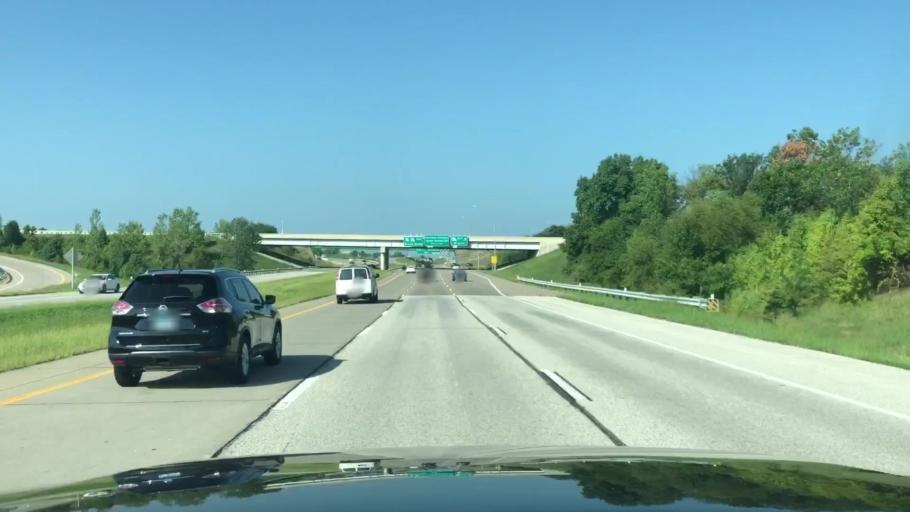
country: US
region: Missouri
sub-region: Saint Charles County
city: Saint Charles
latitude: 38.7576
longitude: -90.5403
